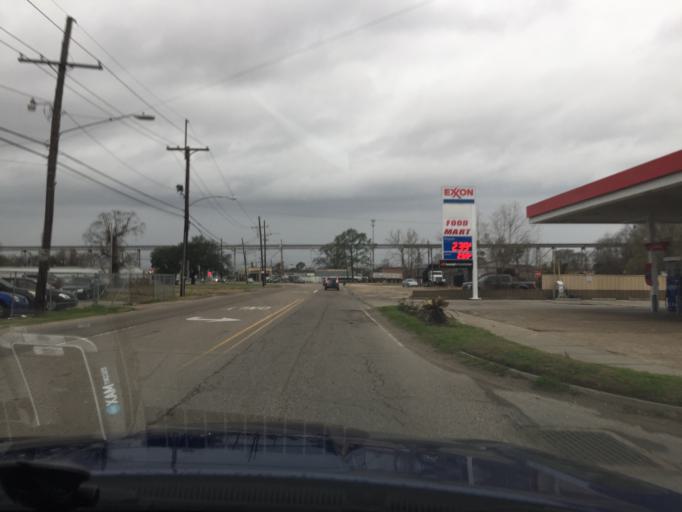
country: US
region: Louisiana
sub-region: Jefferson Parish
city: Bridge City
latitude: 29.9296
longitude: -90.1601
